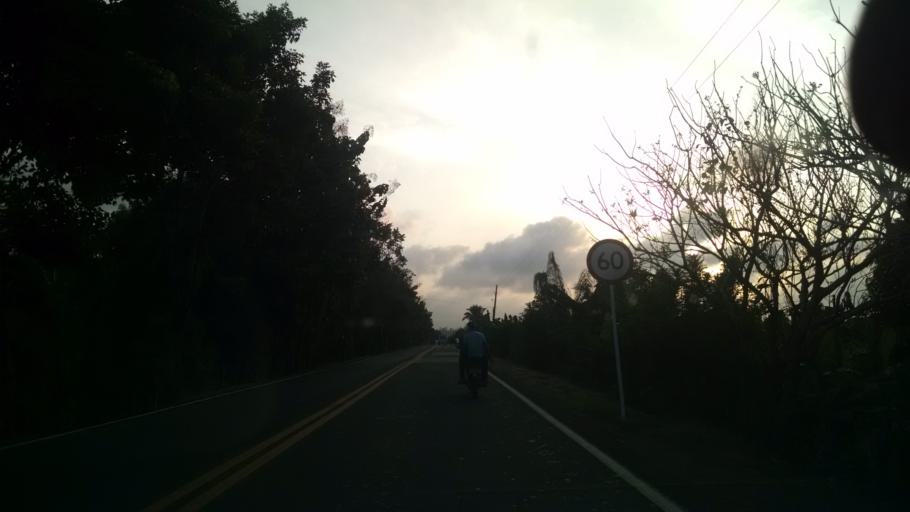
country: CO
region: Antioquia
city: San Juan de Uraba
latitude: 8.7222
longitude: -76.5943
